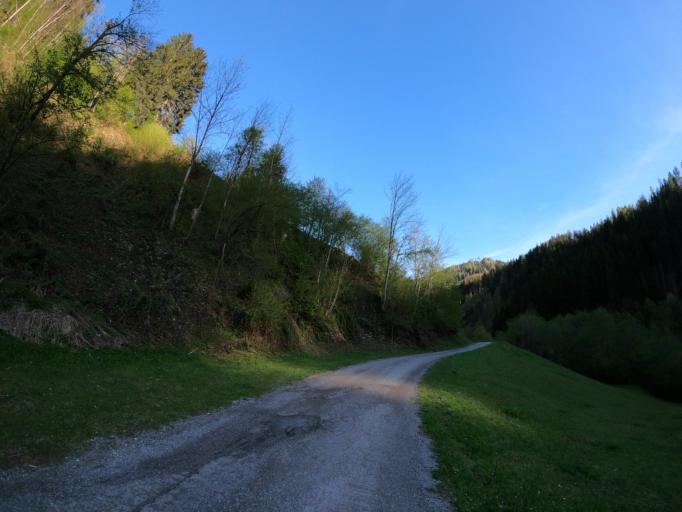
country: AT
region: Salzburg
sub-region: Politischer Bezirk Sankt Johann im Pongau
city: Sankt Johann im Pongau
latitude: 47.3399
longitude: 13.2109
